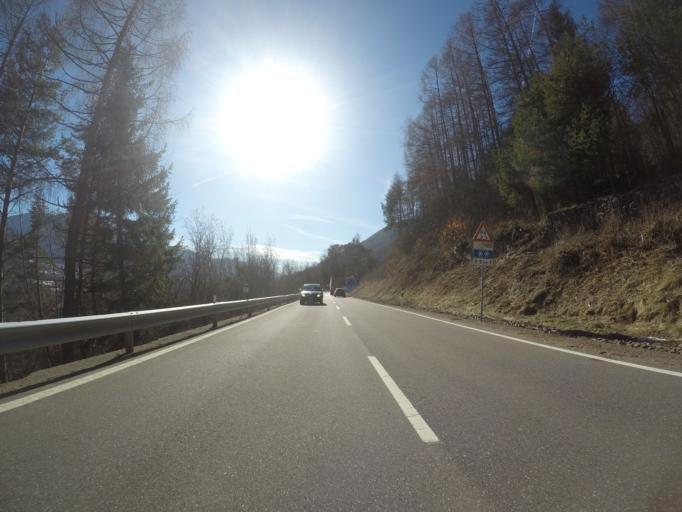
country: IT
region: Trentino-Alto Adige
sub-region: Provincia di Trento
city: Valda
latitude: 46.2061
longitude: 11.2512
